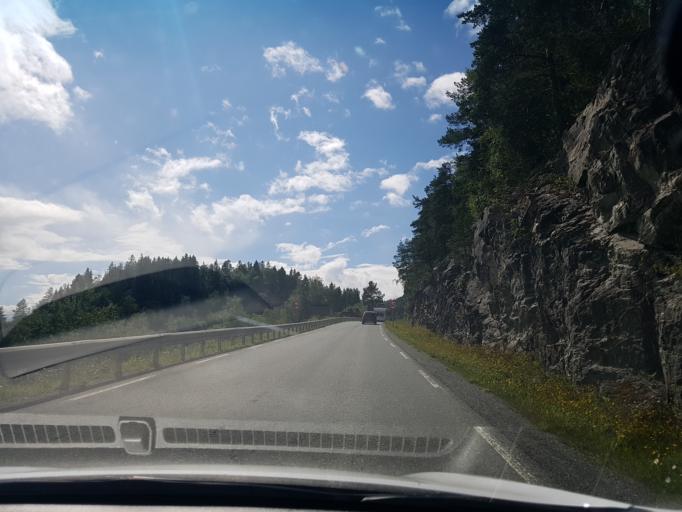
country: NO
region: Nord-Trondelag
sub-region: Frosta
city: Frosta
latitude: 63.5984
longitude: 10.8500
